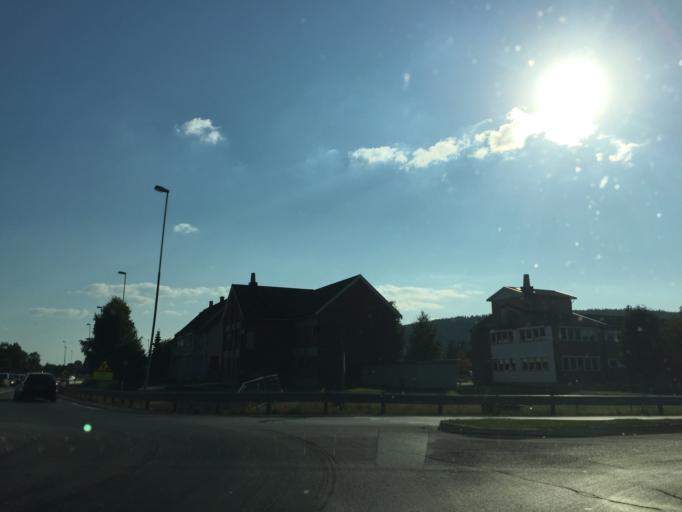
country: NO
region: Hedmark
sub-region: Sor-Odal
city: Skarnes
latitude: 60.2577
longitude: 11.6754
